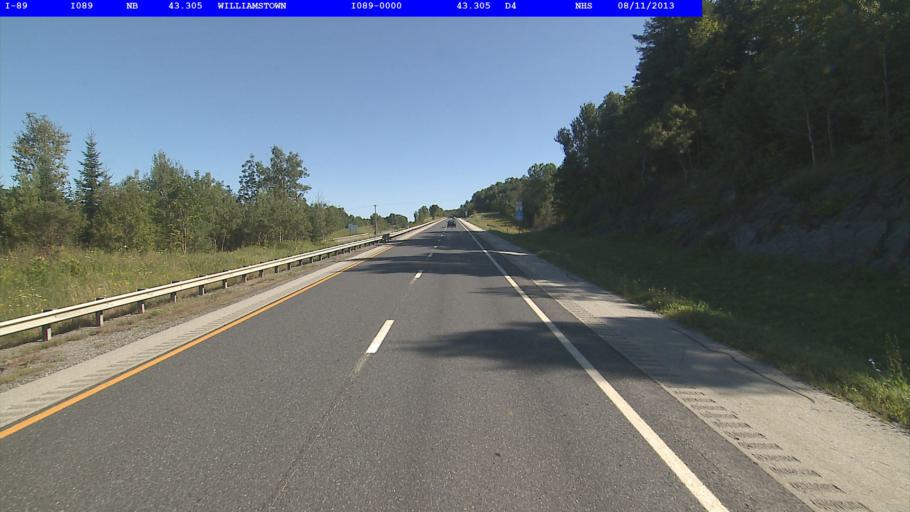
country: US
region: Vermont
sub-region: Washington County
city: Northfield
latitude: 44.1199
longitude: -72.6051
